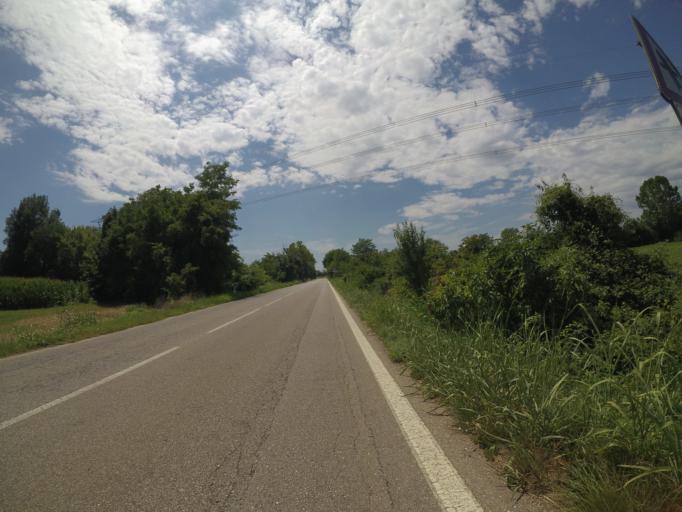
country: IT
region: Friuli Venezia Giulia
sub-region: Provincia di Udine
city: Lestizza
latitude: 45.9665
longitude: 13.1508
